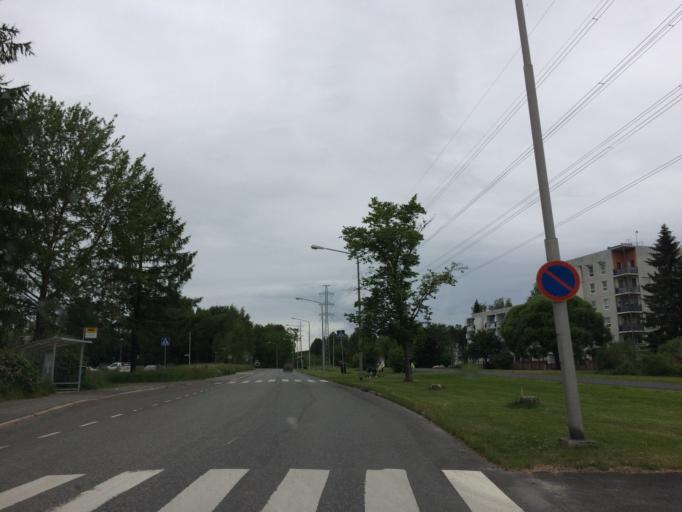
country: FI
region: Haeme
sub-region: Haemeenlinna
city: Haemeenlinna
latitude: 61.0092
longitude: 24.5056
